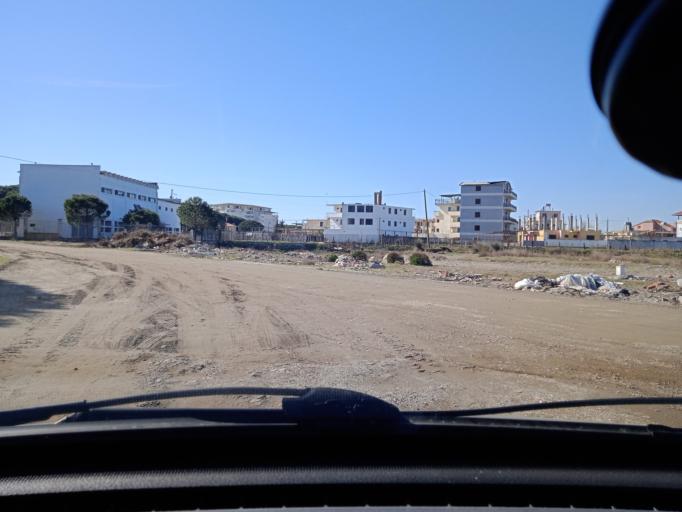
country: AL
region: Shkoder
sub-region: Rrethi i Shkodres
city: Velipoje
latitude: 41.8648
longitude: 19.4426
